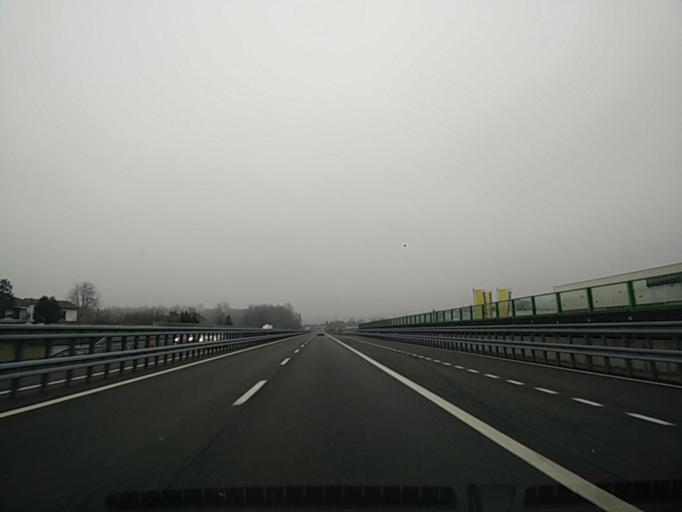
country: IT
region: Piedmont
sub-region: Provincia di Asti
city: Cantarana
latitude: 44.9081
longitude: 8.0506
